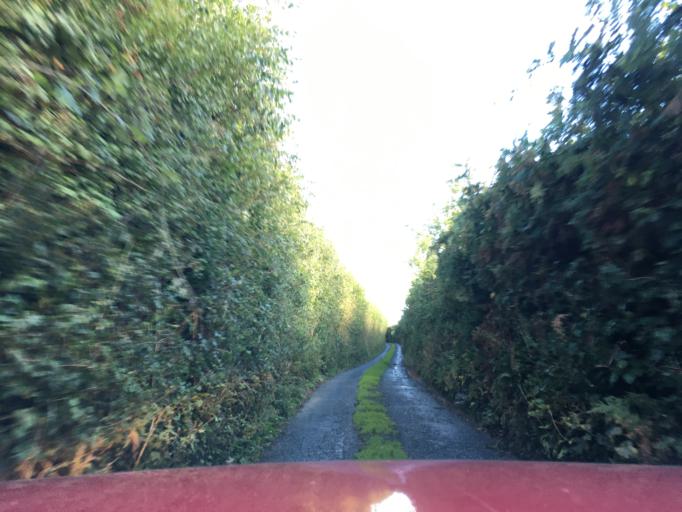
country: GB
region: England
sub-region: Devon
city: Dartmouth
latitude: 50.3351
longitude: -3.6024
